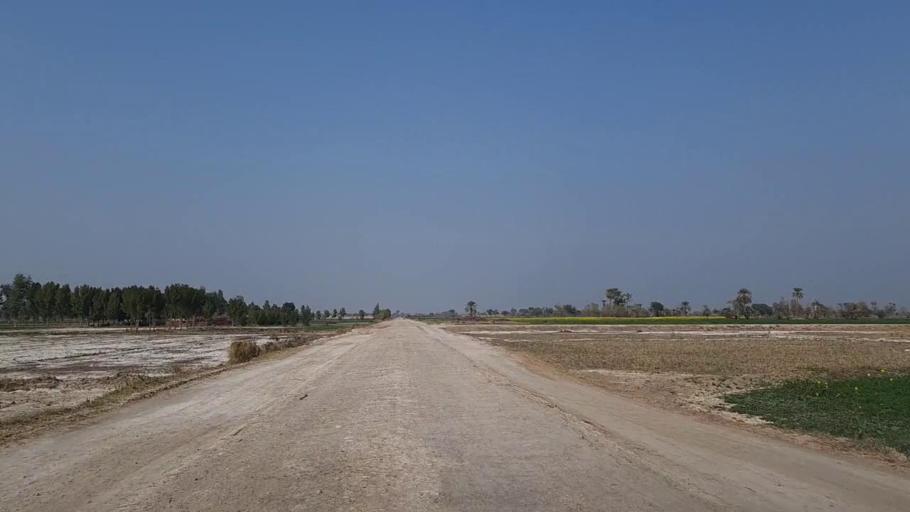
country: PK
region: Sindh
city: Daur
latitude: 26.4128
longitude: 68.4087
